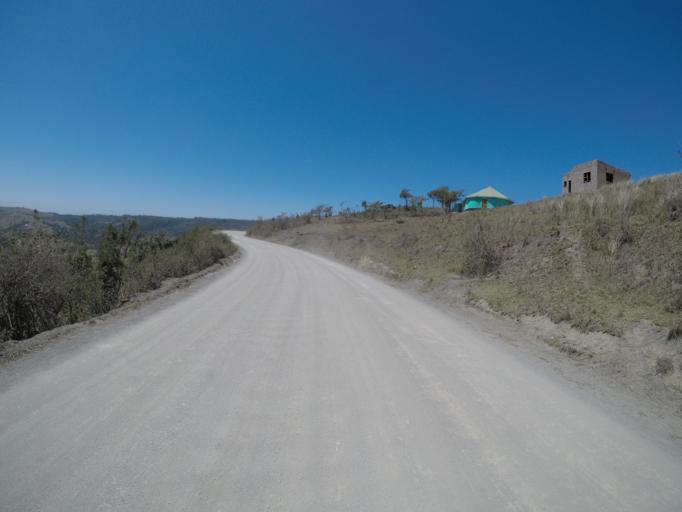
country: ZA
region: Eastern Cape
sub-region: OR Tambo District Municipality
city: Libode
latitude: -31.9982
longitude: 29.0655
